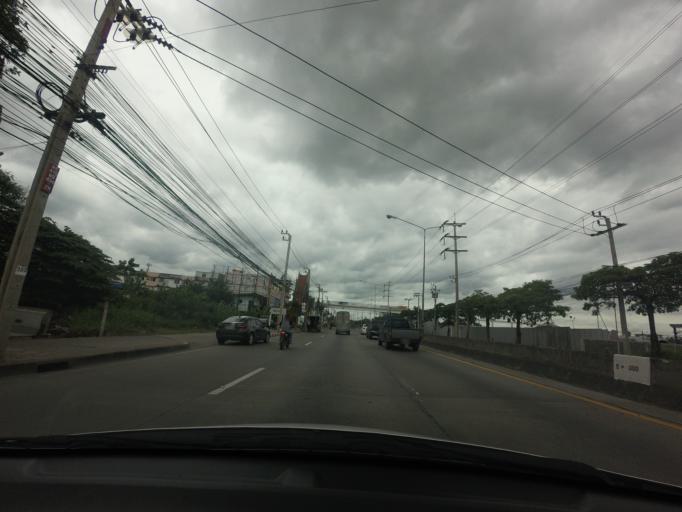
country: TH
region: Bangkok
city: Min Buri
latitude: 13.7768
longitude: 100.7464
